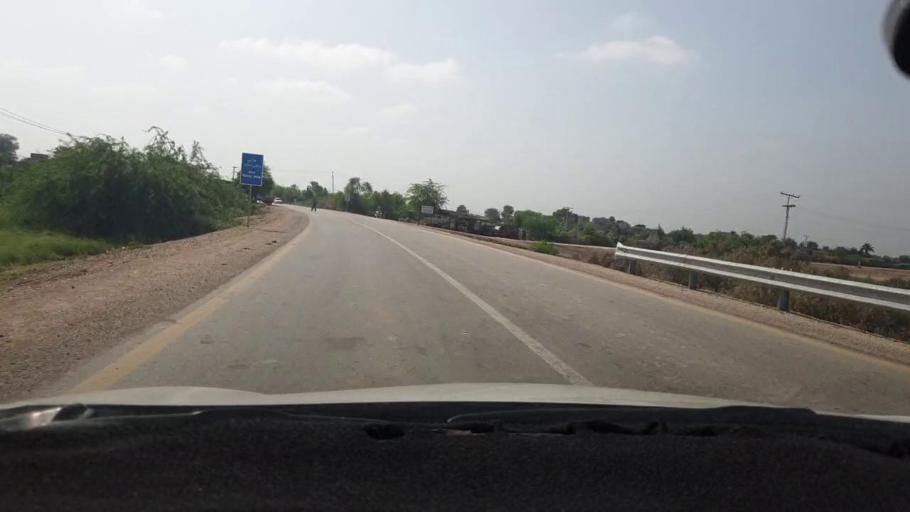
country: PK
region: Sindh
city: Mirpur Khas
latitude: 25.7475
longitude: 69.0846
